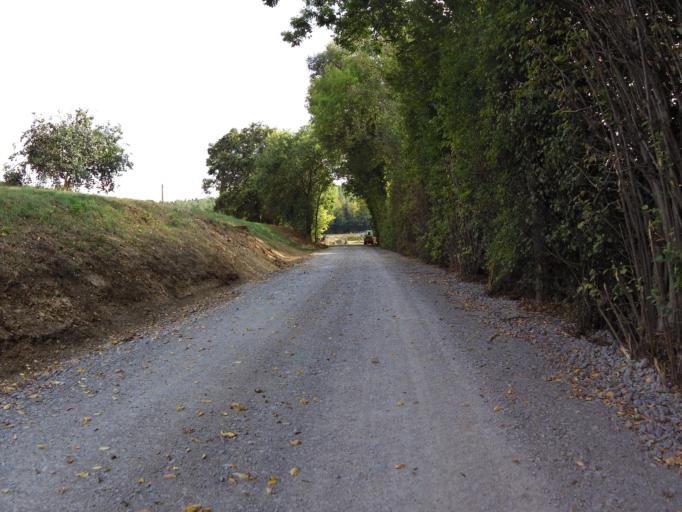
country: DE
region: Bavaria
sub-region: Regierungsbezirk Unterfranken
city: Waldbrunn
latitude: 49.7802
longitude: 9.8027
